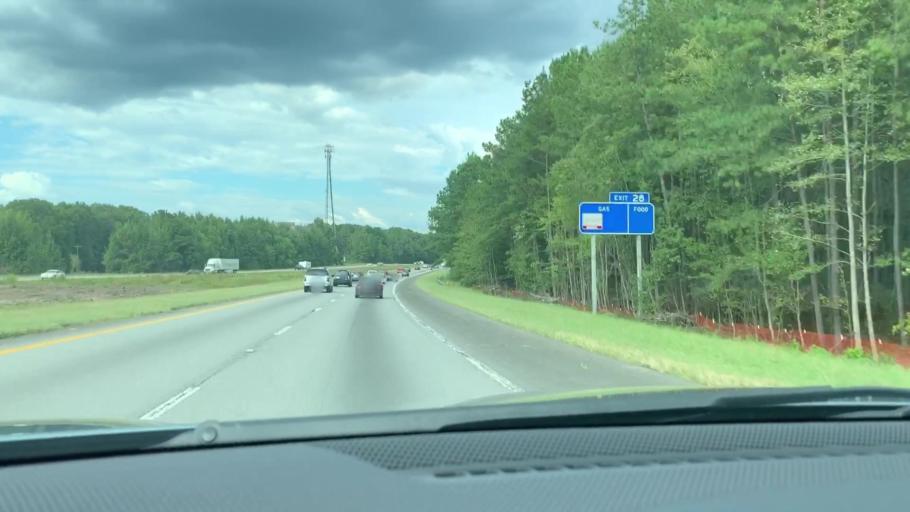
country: US
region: South Carolina
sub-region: Jasper County
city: Ridgeland
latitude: 32.5709
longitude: -80.9381
